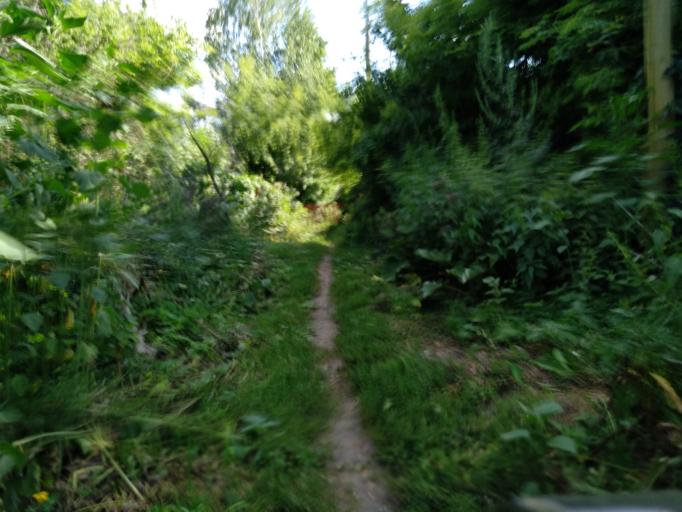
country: RU
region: Lipetsk
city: Dobrinka
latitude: 52.0389
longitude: 40.5497
